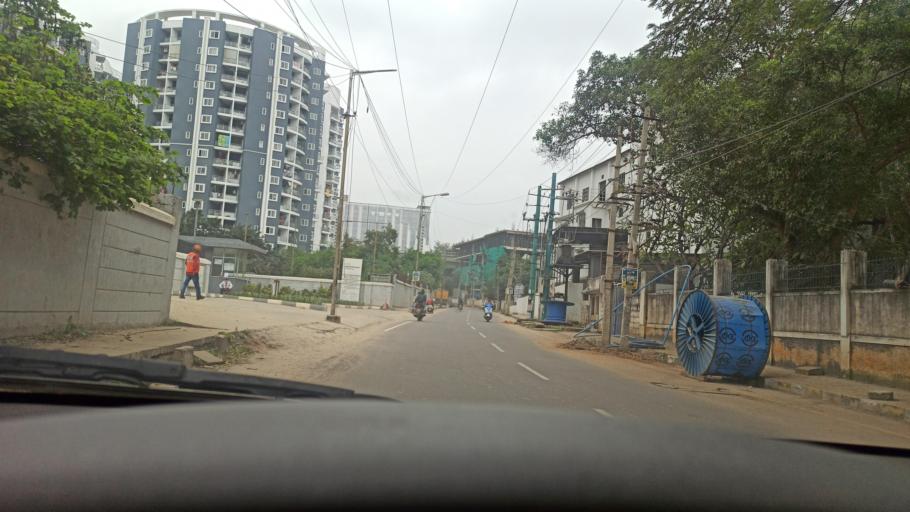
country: IN
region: Karnataka
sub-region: Bangalore Urban
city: Bangalore
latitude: 12.9955
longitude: 77.6898
